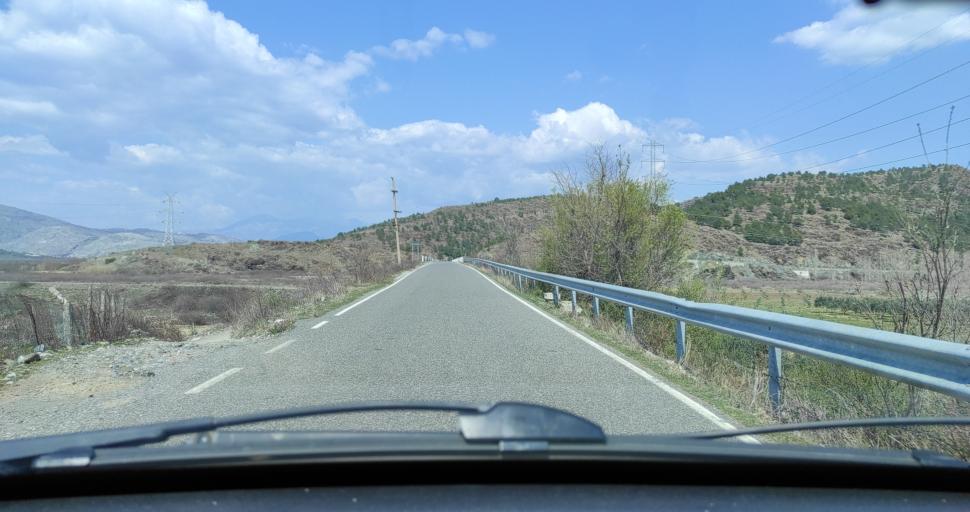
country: AL
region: Shkoder
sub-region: Rrethi i Shkodres
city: Hajmel
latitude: 41.9762
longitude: 19.6450
